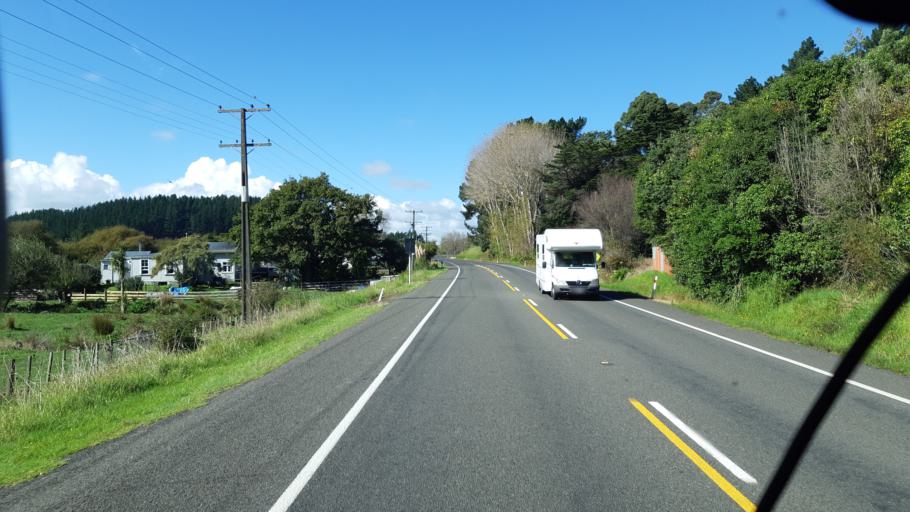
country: NZ
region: Manawatu-Wanganui
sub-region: Wanganui District
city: Wanganui
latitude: -39.9598
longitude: 175.0944
